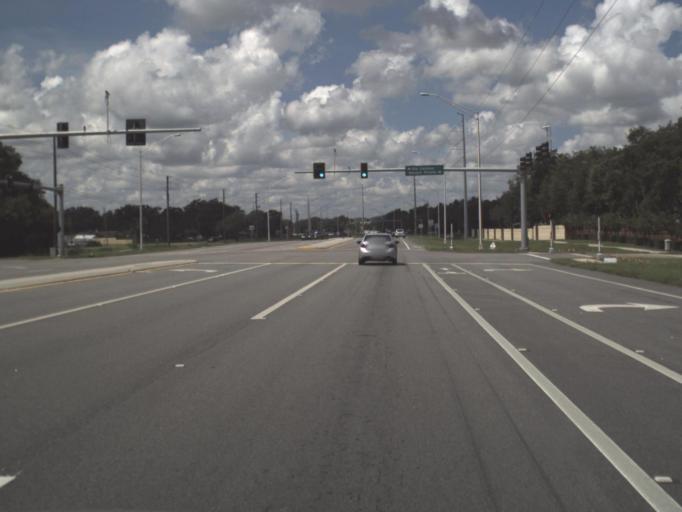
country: US
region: Florida
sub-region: Polk County
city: Gibsonia
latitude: 28.1079
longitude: -81.9335
